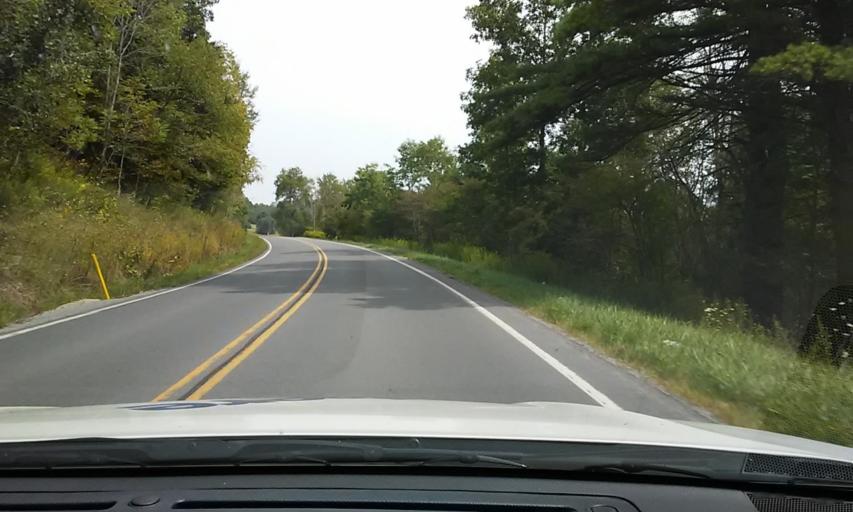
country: US
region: Pennsylvania
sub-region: Elk County
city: Ridgway
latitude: 41.3016
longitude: -78.6648
